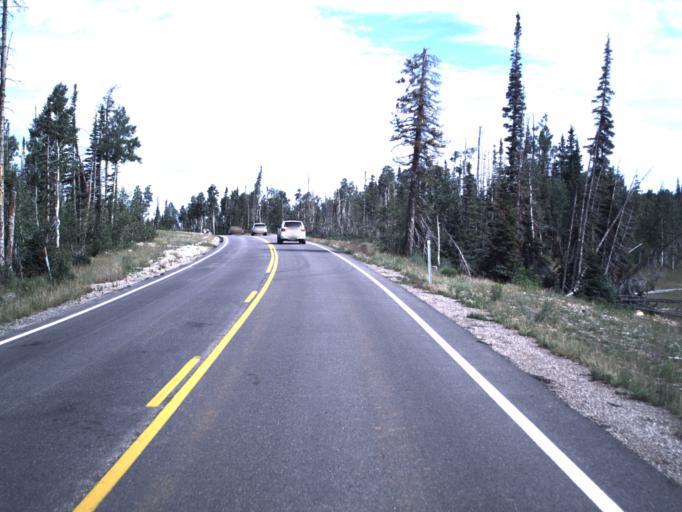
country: US
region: Utah
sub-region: Iron County
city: Parowan
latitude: 37.5500
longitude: -112.7864
